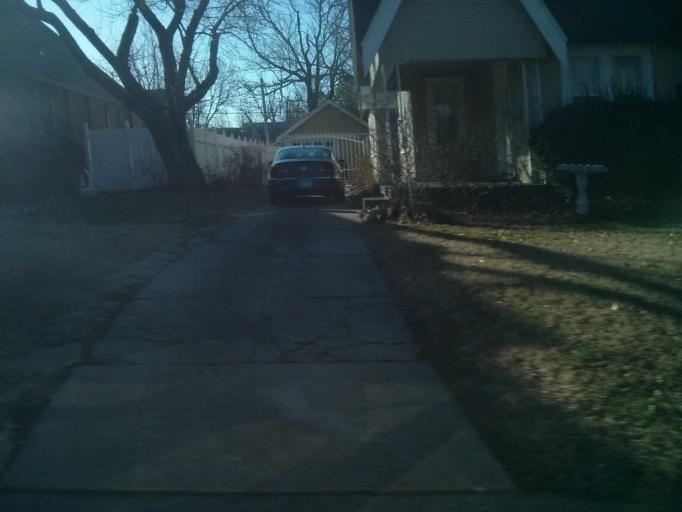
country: US
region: Oklahoma
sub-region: Tulsa County
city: Tulsa
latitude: 36.1563
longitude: -95.9433
